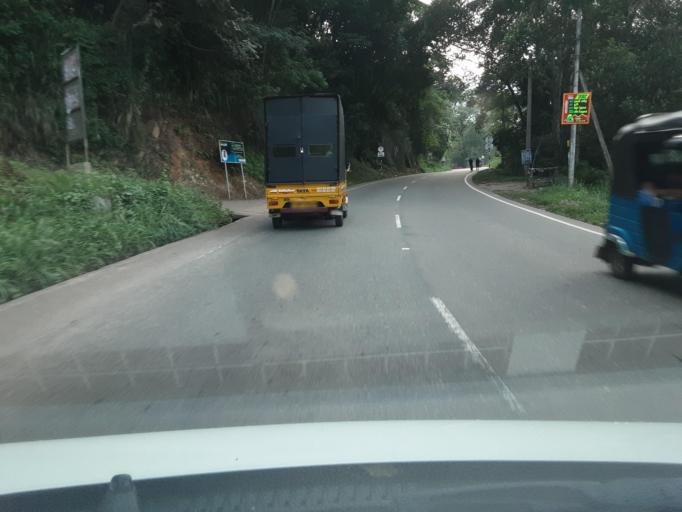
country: LK
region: Uva
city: Badulla
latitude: 6.9545
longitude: 81.0289
